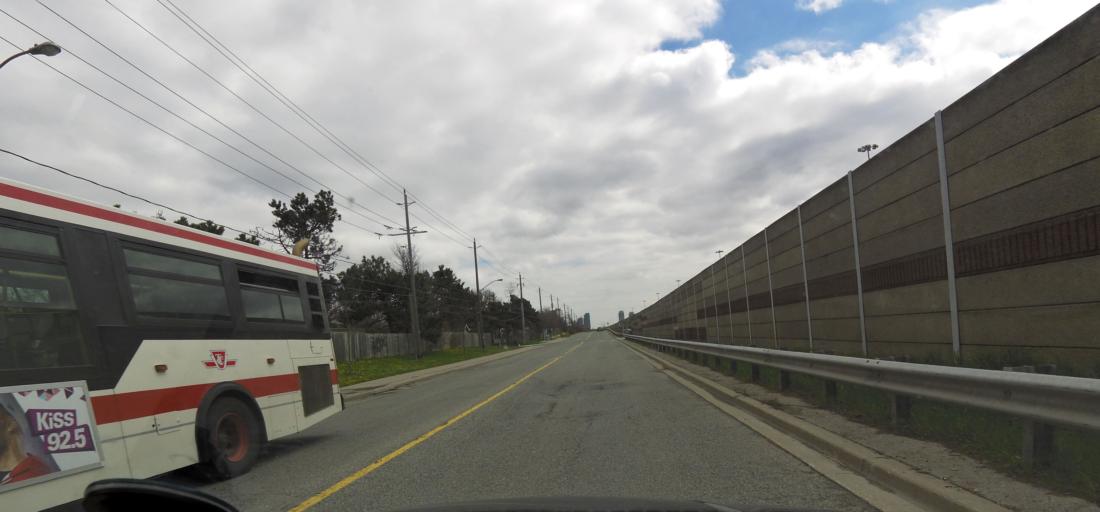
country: CA
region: Ontario
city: Etobicoke
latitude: 43.6635
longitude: -79.5710
